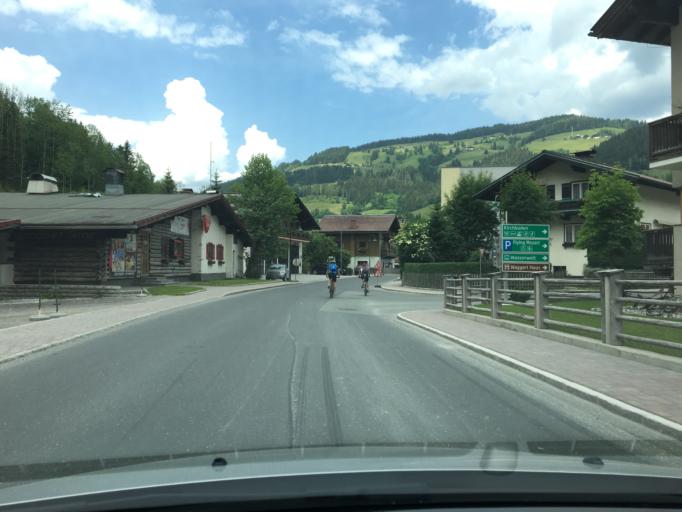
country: AT
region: Salzburg
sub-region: Politischer Bezirk Sankt Johann im Pongau
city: Wagrain
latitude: 47.3304
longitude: 13.2984
